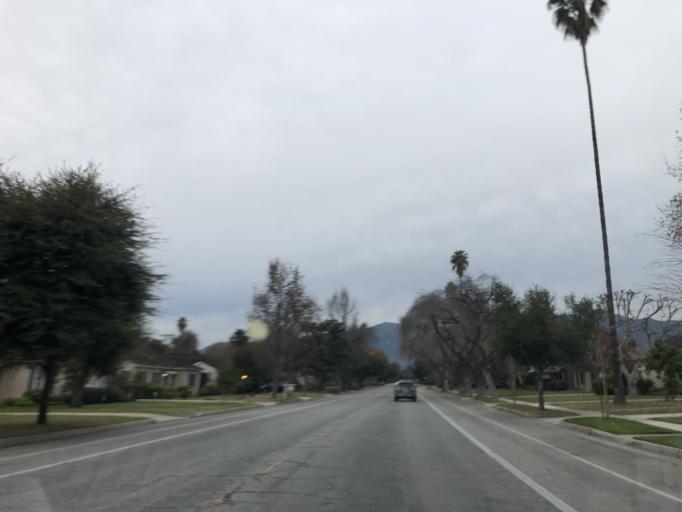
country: US
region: California
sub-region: Los Angeles County
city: San Marino
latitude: 34.1147
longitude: -118.0999
